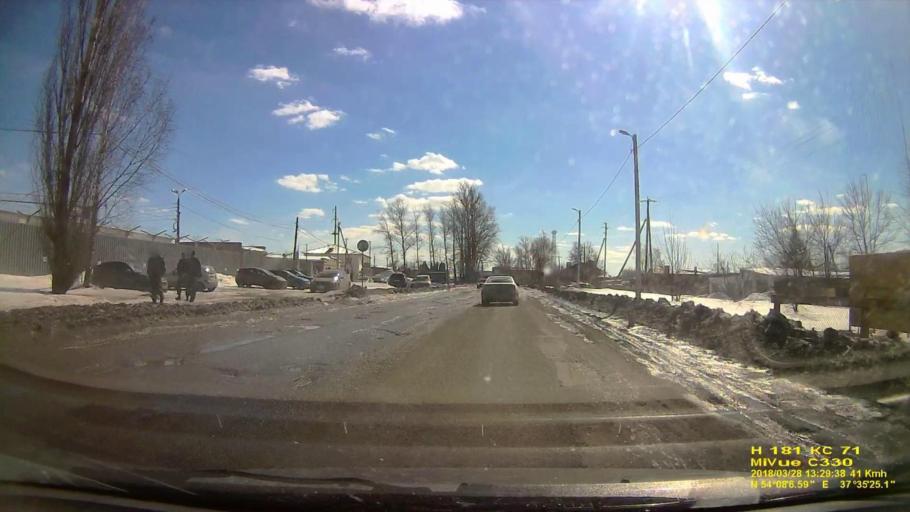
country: RU
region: Tula
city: Mendeleyevskiy
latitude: 54.1350
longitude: 37.5903
